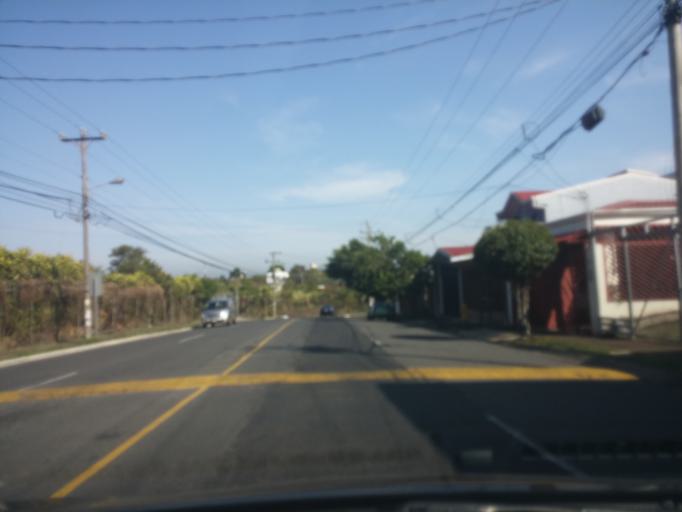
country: CR
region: Heredia
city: Llorente
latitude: 9.9942
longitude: -84.1538
